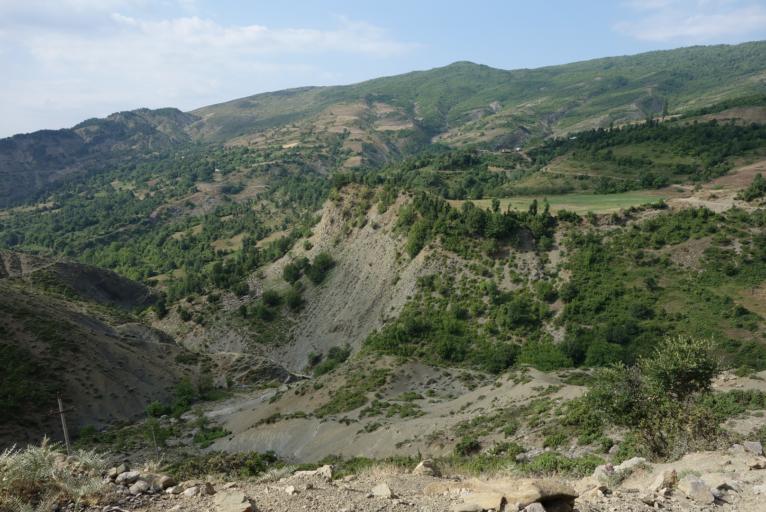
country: AL
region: Gjirokaster
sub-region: Rrethi i Permetit
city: Frasher
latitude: 40.3312
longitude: 20.4475
